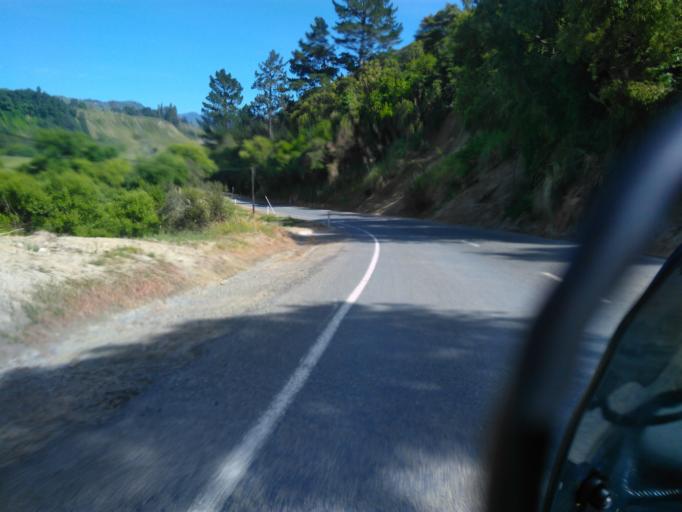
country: NZ
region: Hawke's Bay
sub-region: Wairoa District
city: Wairoa
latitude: -38.8647
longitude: 177.1984
